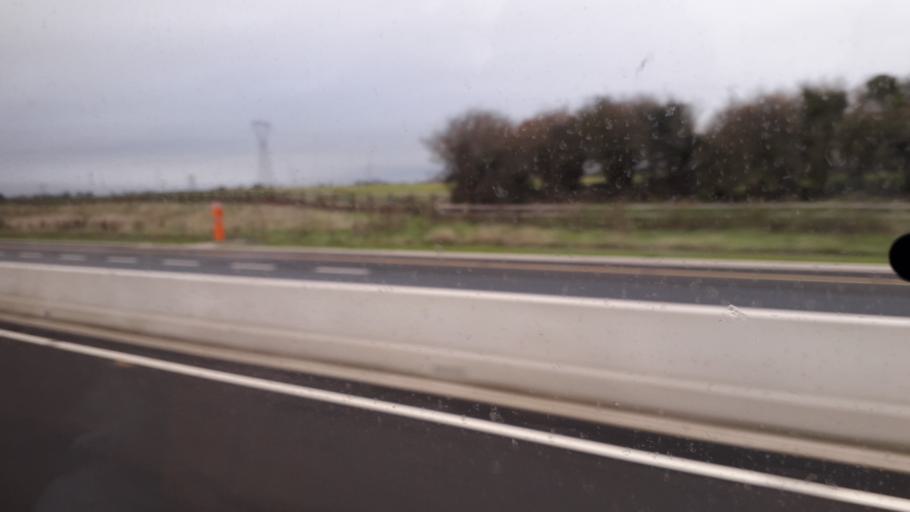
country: IE
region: Connaught
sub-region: County Galway
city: Athenry
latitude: 53.2876
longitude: -8.8061
